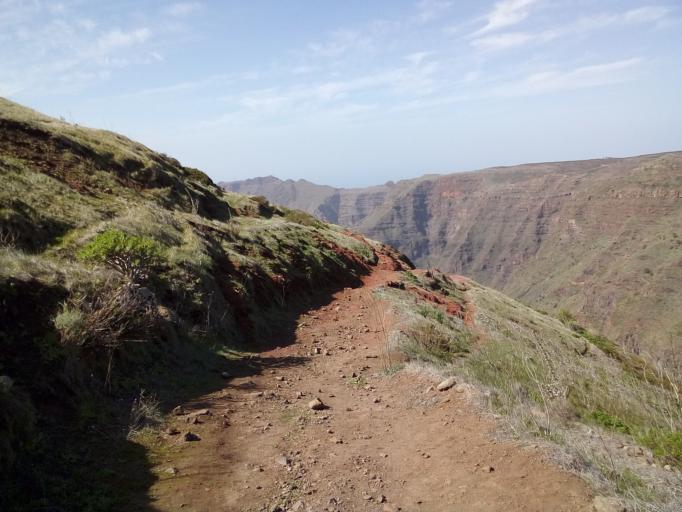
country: ES
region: Canary Islands
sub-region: Provincia de Santa Cruz de Tenerife
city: Vallehermosa
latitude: 28.1174
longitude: -17.2924
